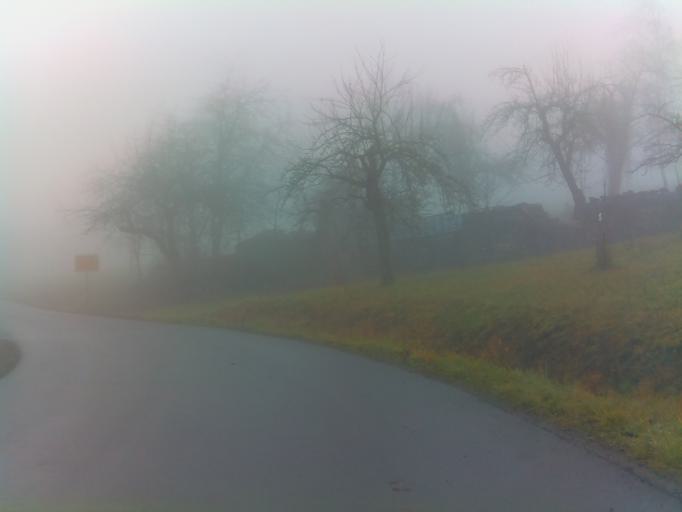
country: DE
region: Bavaria
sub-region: Regierungsbezirk Unterfranken
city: Kreuzwertheim
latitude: 49.7449
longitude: 9.5736
